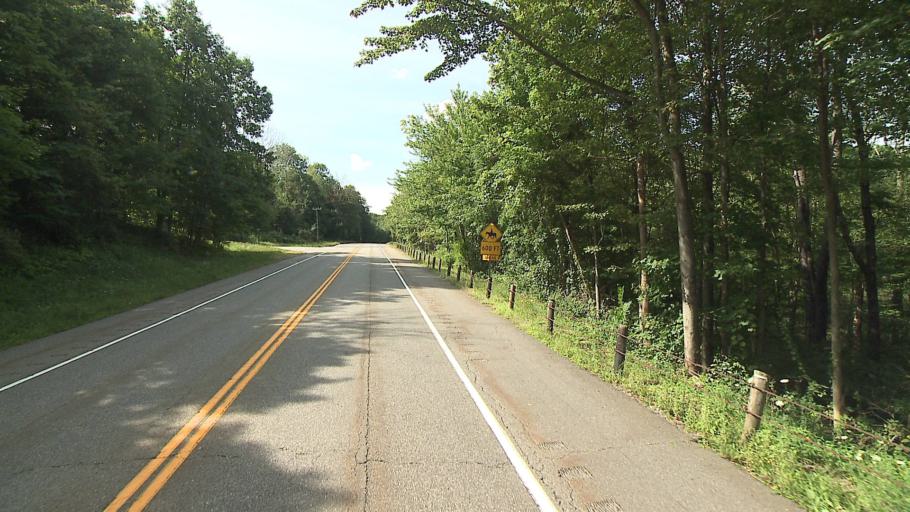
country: US
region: Connecticut
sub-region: Litchfield County
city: Litchfield
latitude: 41.7492
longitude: -73.1615
